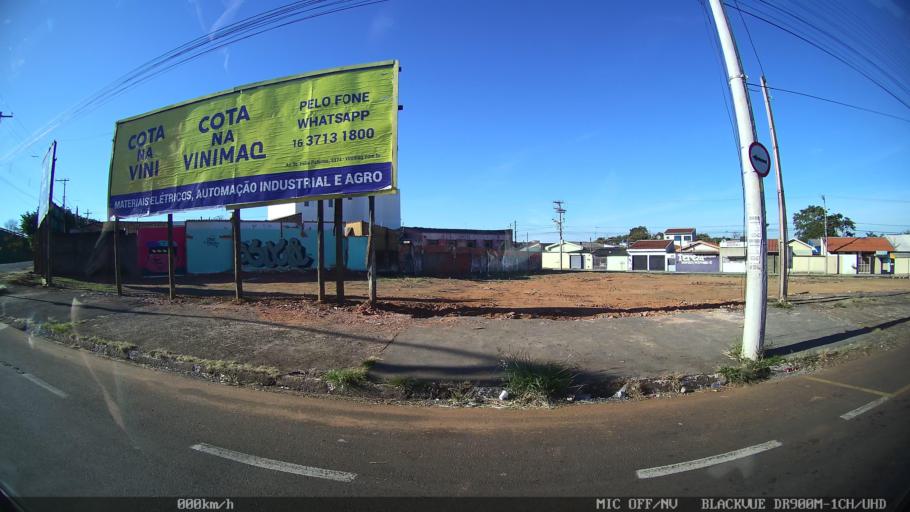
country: BR
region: Sao Paulo
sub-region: Franca
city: Franca
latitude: -20.5740
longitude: -47.3727
